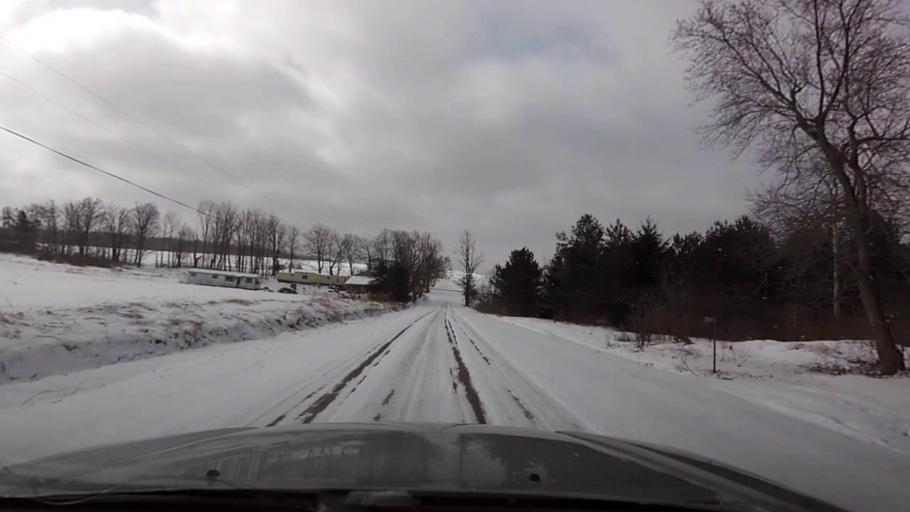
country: US
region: New York
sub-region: Cattaraugus County
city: Franklinville
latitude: 42.3064
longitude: -78.3538
